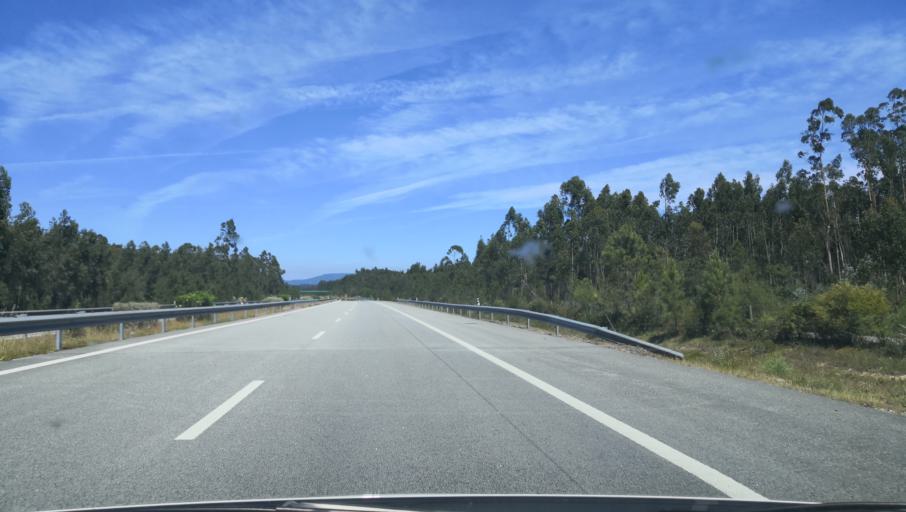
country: PT
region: Coimbra
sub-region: Montemor-O-Velho
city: Arazede
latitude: 40.2733
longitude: -8.5990
